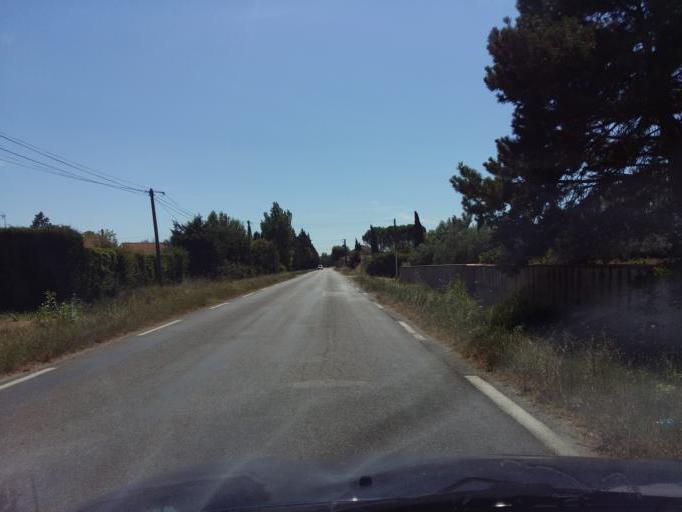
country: FR
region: Provence-Alpes-Cote d'Azur
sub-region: Departement du Vaucluse
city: Sarrians
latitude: 44.0897
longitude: 4.9848
